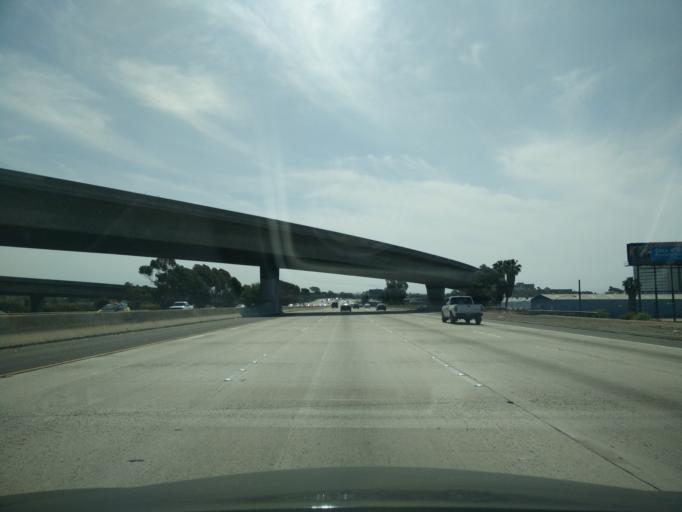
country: US
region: California
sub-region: San Diego County
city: National City
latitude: 32.6924
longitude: -117.1210
